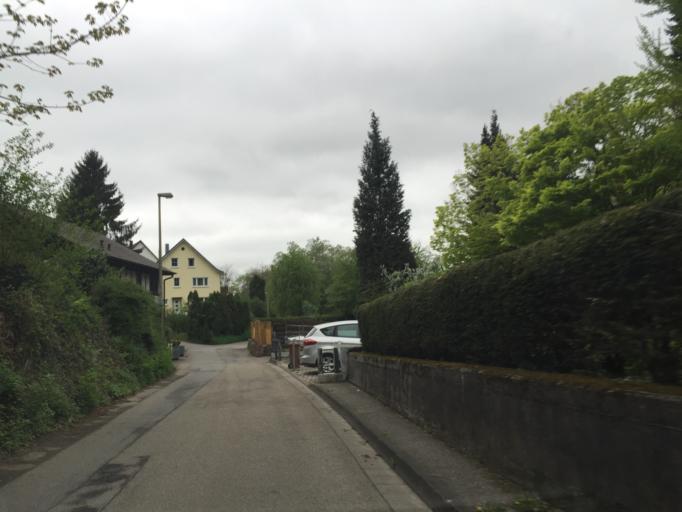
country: DE
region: Baden-Wuerttemberg
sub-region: Karlsruhe Region
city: Weinheim
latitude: 49.5264
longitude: 8.6760
